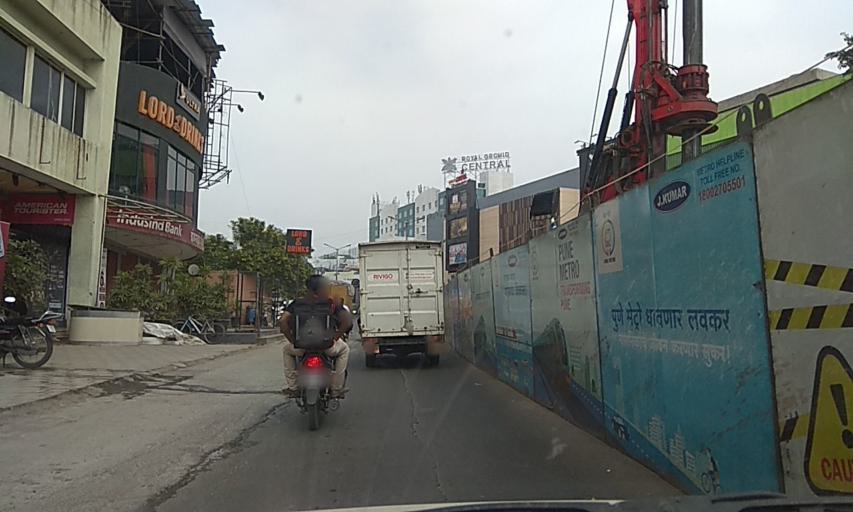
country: IN
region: Maharashtra
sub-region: Pune Division
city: Shivaji Nagar
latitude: 18.5447
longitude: 73.9057
